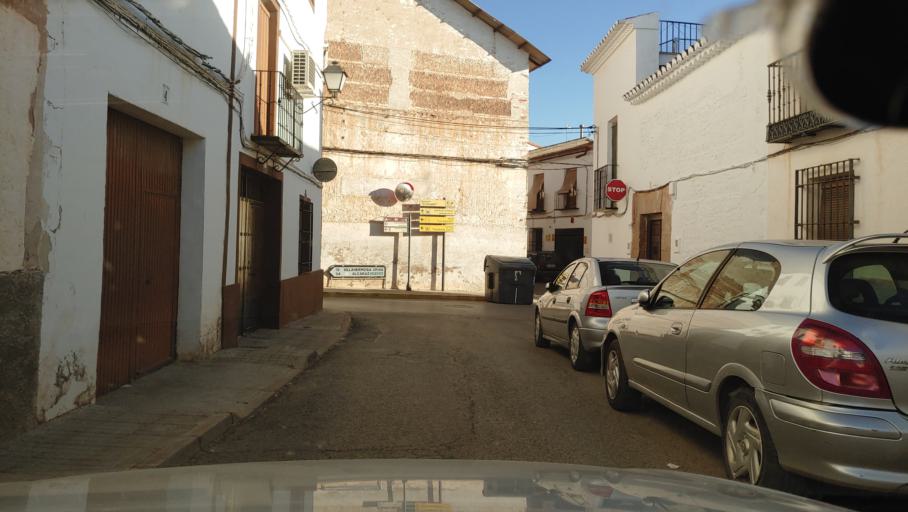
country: ES
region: Castille-La Mancha
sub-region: Provincia de Ciudad Real
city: Infantes
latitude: 38.7385
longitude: -3.0122
